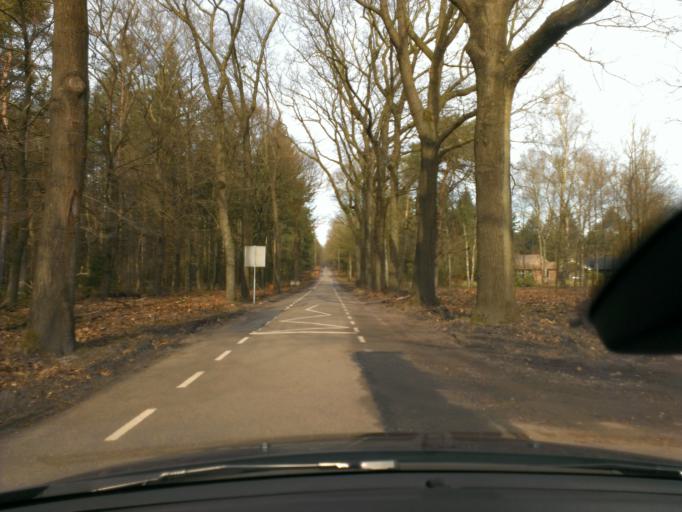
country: NL
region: Gelderland
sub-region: Gemeente Epe
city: Epe
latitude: 52.3852
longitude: 5.9688
